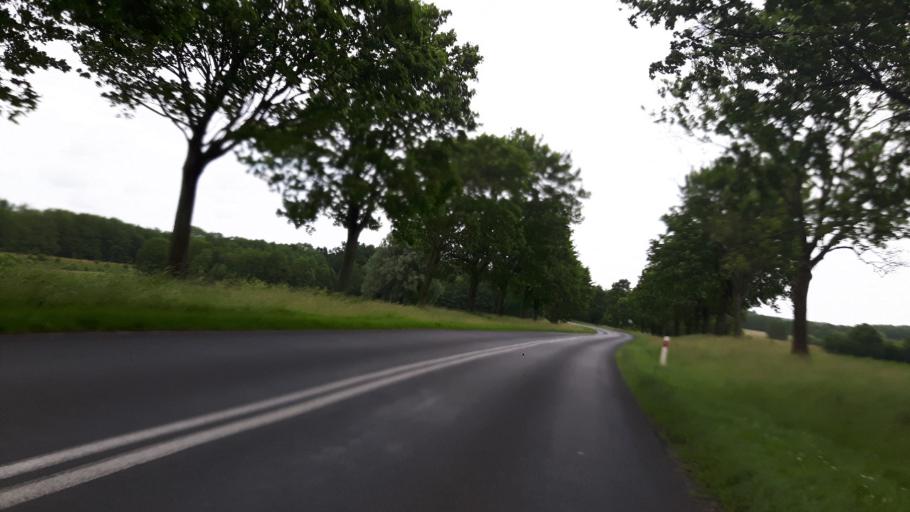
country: PL
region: West Pomeranian Voivodeship
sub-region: Powiat gryficki
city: Gryfice
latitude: 53.9614
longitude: 15.2279
